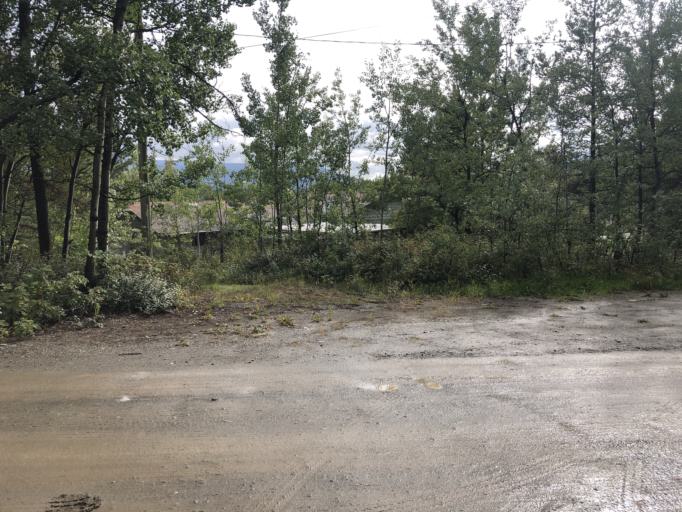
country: CA
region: Yukon
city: Whitehorse
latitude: 60.8793
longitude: -135.3582
